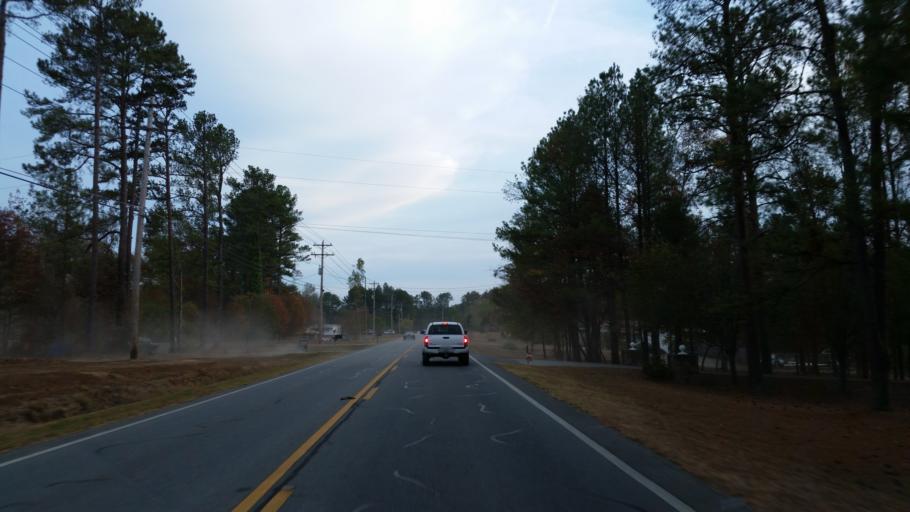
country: US
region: Georgia
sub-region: Gordon County
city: Calhoun
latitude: 34.5983
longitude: -84.9116
